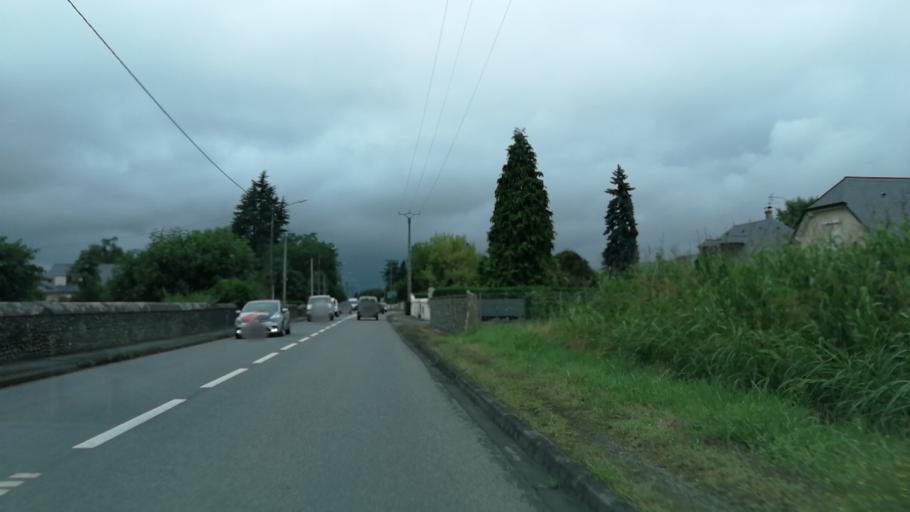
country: FR
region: Aquitaine
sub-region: Departement des Pyrenees-Atlantiques
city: Oloron-Sainte-Marie
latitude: 43.1592
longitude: -0.5984
